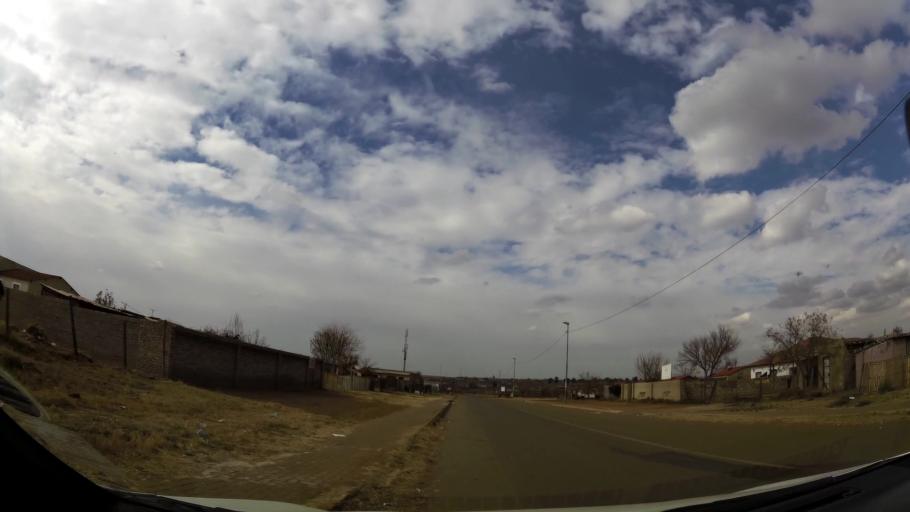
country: ZA
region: Gauteng
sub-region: Ekurhuleni Metropolitan Municipality
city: Germiston
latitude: -26.4084
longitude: 28.1624
